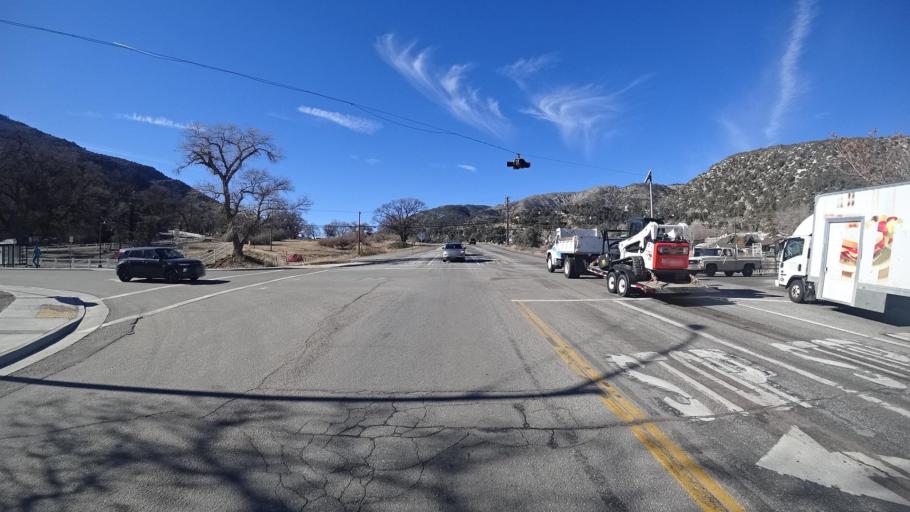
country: US
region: California
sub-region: Kern County
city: Frazier Park
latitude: 34.8207
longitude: -118.9456
